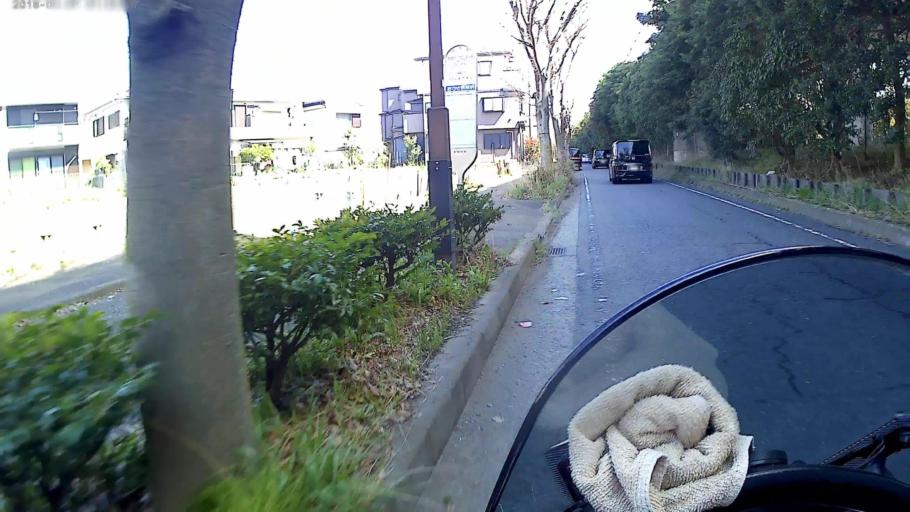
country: JP
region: Kanagawa
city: Chigasaki
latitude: 35.3471
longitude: 139.4285
